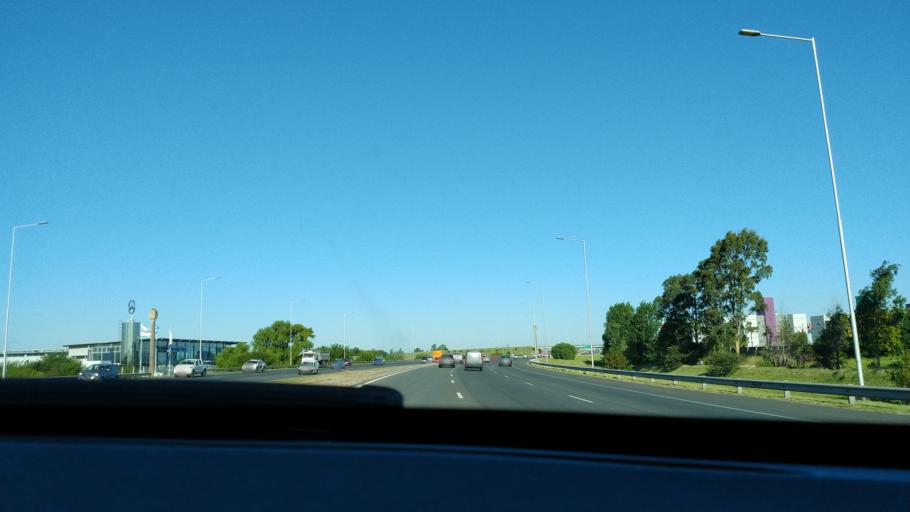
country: AR
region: Cordoba
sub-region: Departamento de Capital
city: Cordoba
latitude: -31.3535
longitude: -64.1963
